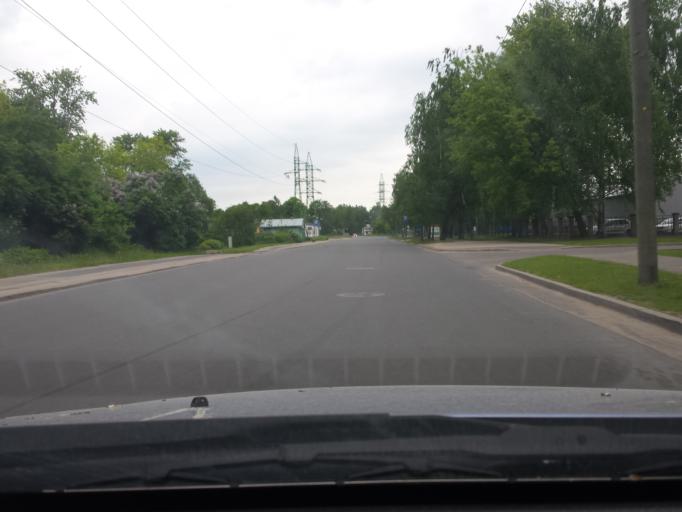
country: LV
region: Riga
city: Jaunciems
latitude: 56.9888
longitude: 24.1863
